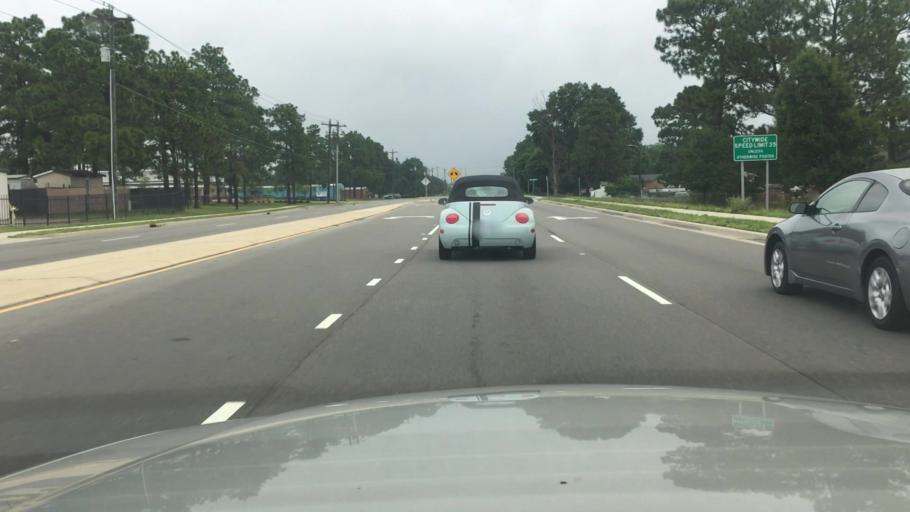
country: US
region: North Carolina
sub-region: Cumberland County
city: Fayetteville
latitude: 35.0105
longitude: -78.9104
